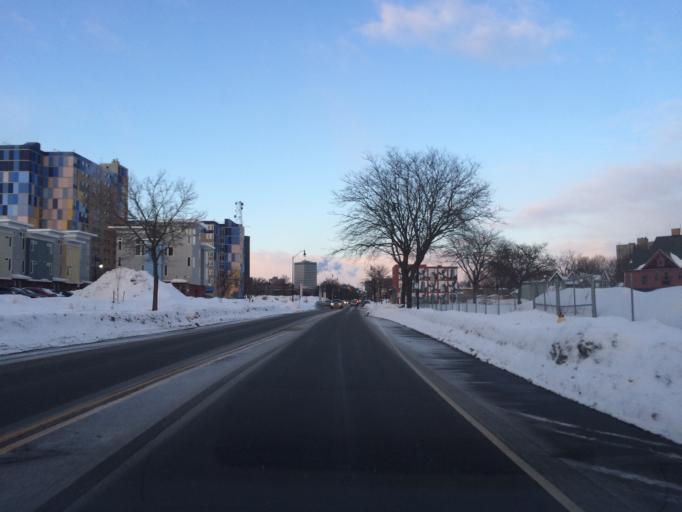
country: US
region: New York
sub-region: Monroe County
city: Rochester
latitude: 43.1441
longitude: -77.6109
